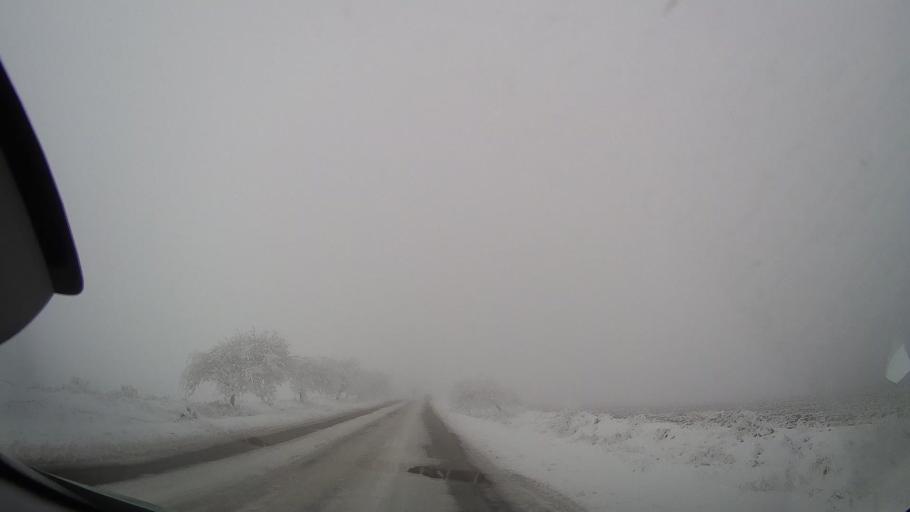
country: RO
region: Neamt
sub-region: Comuna Valea Ursului
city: Valea Ursului
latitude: 46.8249
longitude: 27.0624
